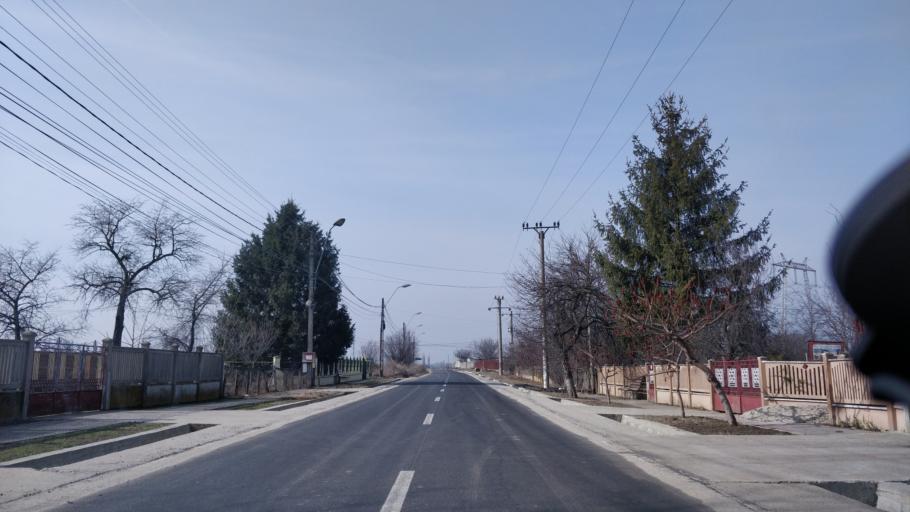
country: RO
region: Giurgiu
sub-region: Comuna Bolintin Deal
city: Bolintin Deal
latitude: 44.4619
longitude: 25.8045
